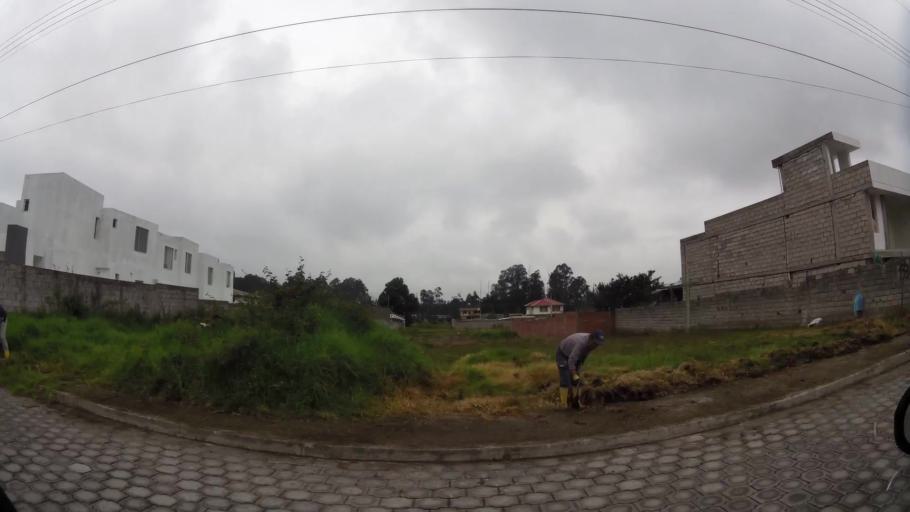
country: EC
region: Pichincha
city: Quito
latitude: -0.2682
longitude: -78.4758
